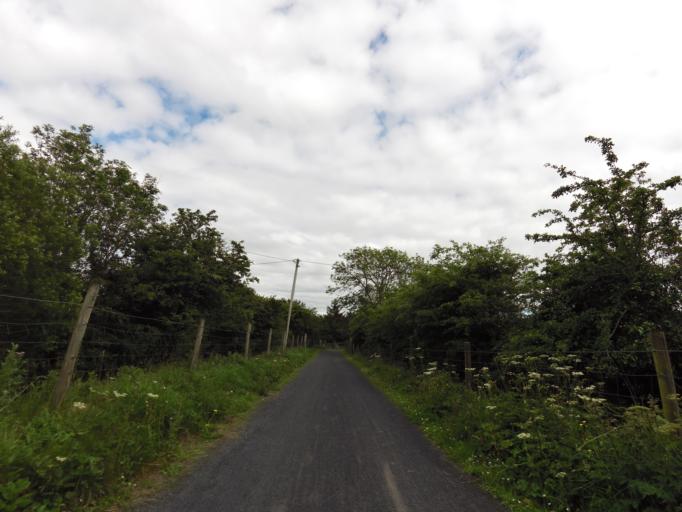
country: IE
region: Connaught
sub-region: Maigh Eo
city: Westport
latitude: 53.8119
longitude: -9.5288
